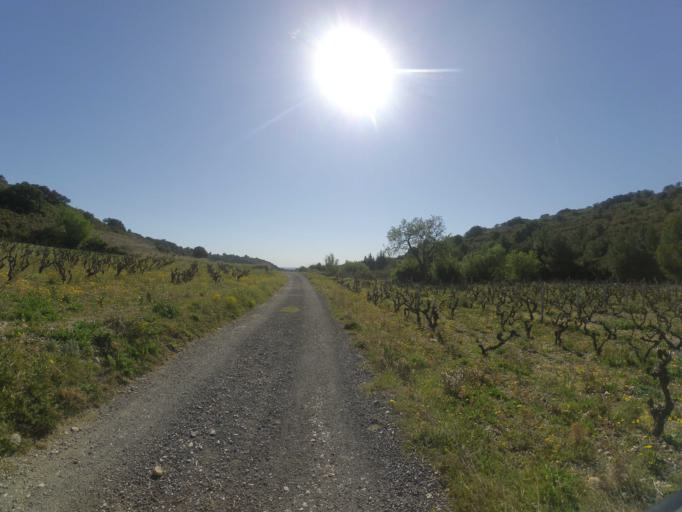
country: FR
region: Languedoc-Roussillon
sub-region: Departement des Pyrenees-Orientales
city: Baixas
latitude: 42.7605
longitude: 2.7852
